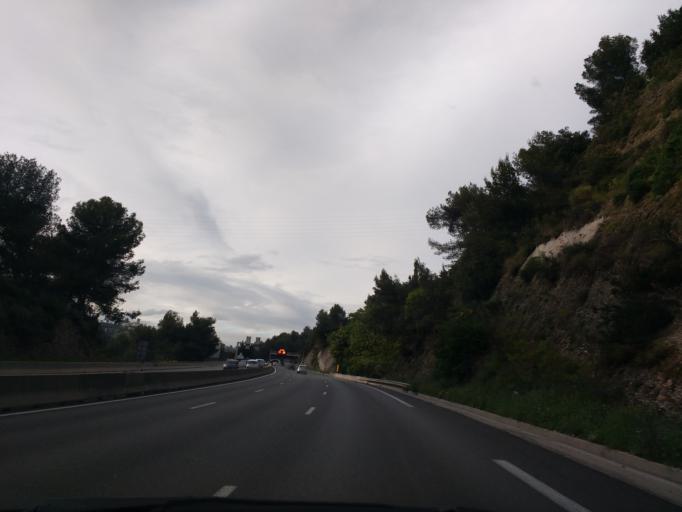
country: FR
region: Provence-Alpes-Cote d'Azur
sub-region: Departement des Alpes-Maritimes
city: Colomars
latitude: 43.7134
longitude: 7.2138
